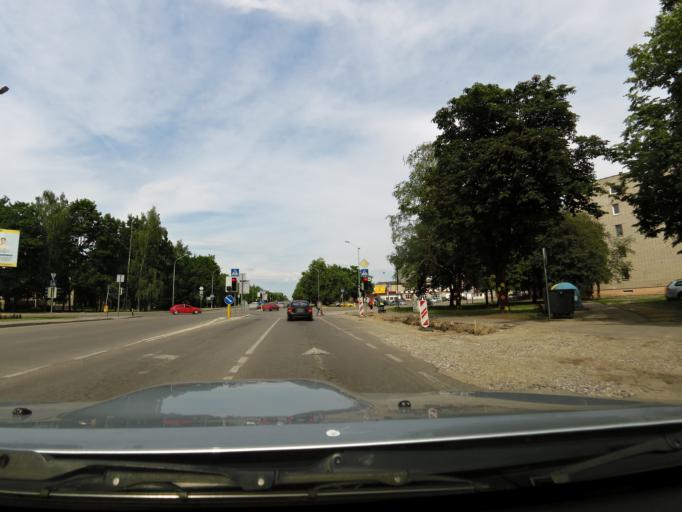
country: LT
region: Marijampoles apskritis
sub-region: Marijampole Municipality
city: Marijampole
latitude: 54.5676
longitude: 23.3600
